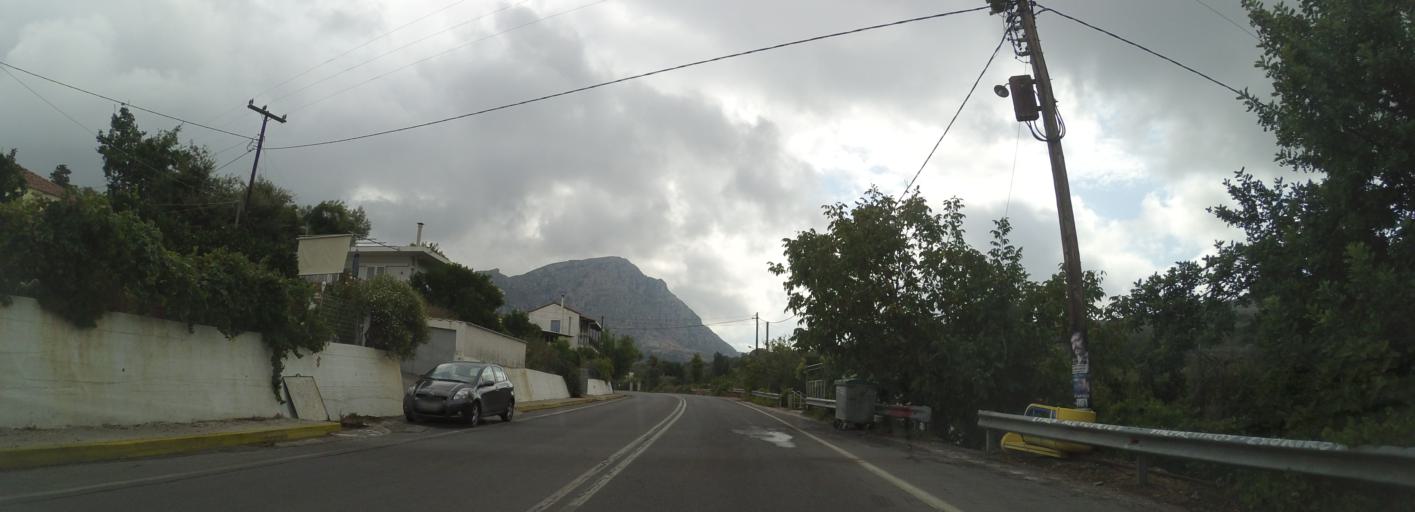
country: GR
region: Crete
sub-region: Nomos Rethymnis
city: Agia Foteini
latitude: 35.2200
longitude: 24.5206
